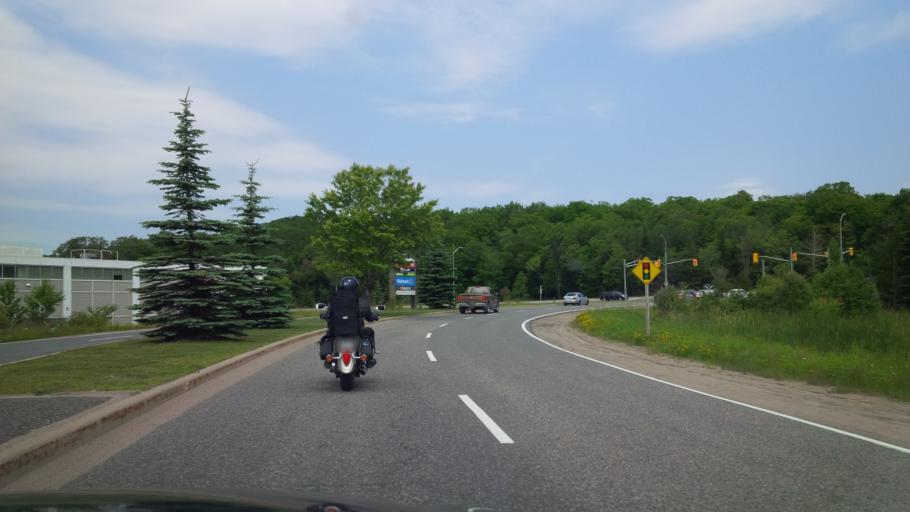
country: CA
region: Ontario
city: Huntsville
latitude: 45.3439
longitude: -79.2255
